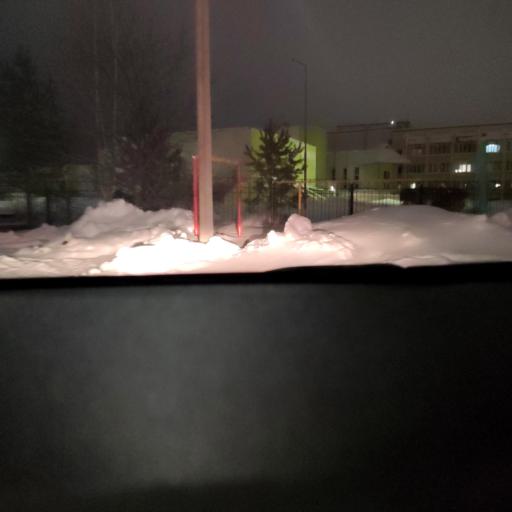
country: RU
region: Tatarstan
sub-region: Chistopol'skiy Rayon
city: Chistopol'
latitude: 55.3593
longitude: 50.5852
